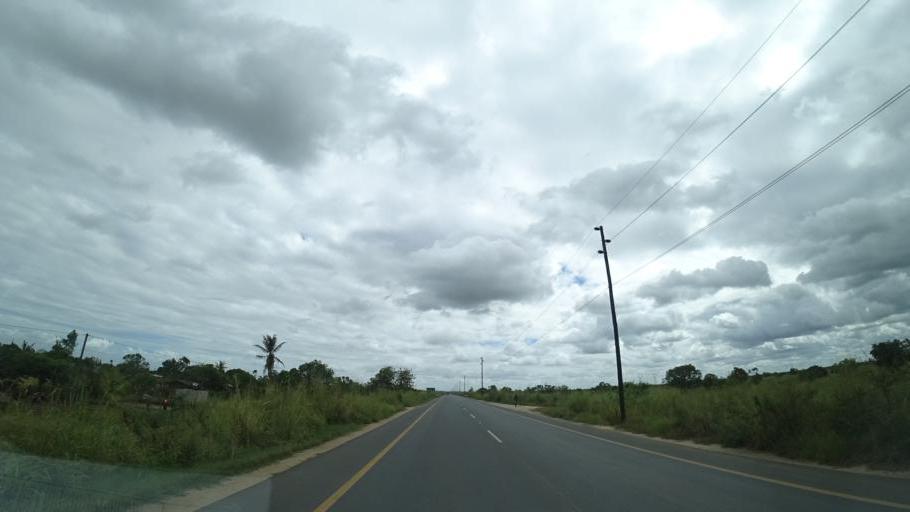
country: MZ
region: Sofala
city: Dondo
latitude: -19.5256
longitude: 34.6250
